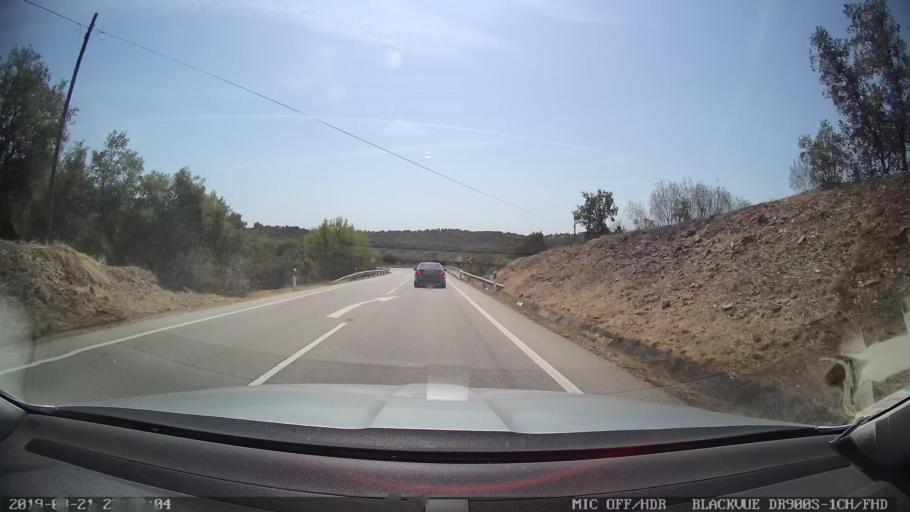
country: PT
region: Castelo Branco
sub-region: Idanha-A-Nova
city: Idanha-a-Nova
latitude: 39.8577
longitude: -7.3430
